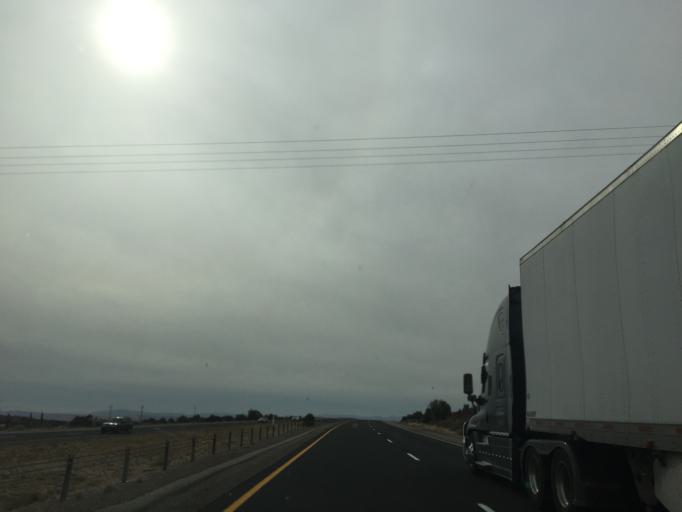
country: US
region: Utah
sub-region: Washington County
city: Toquerville
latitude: 37.2621
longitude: -113.3279
